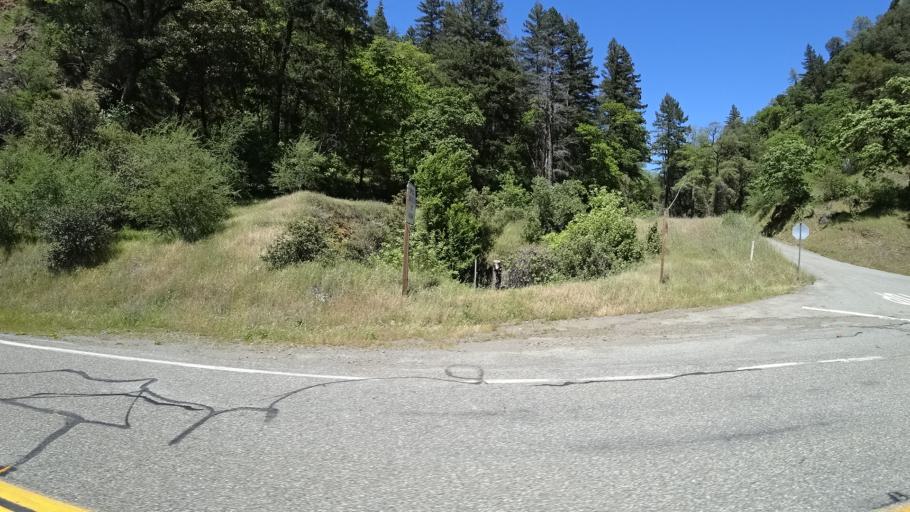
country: US
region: California
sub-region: Trinity County
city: Hayfork
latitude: 40.7619
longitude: -123.2860
